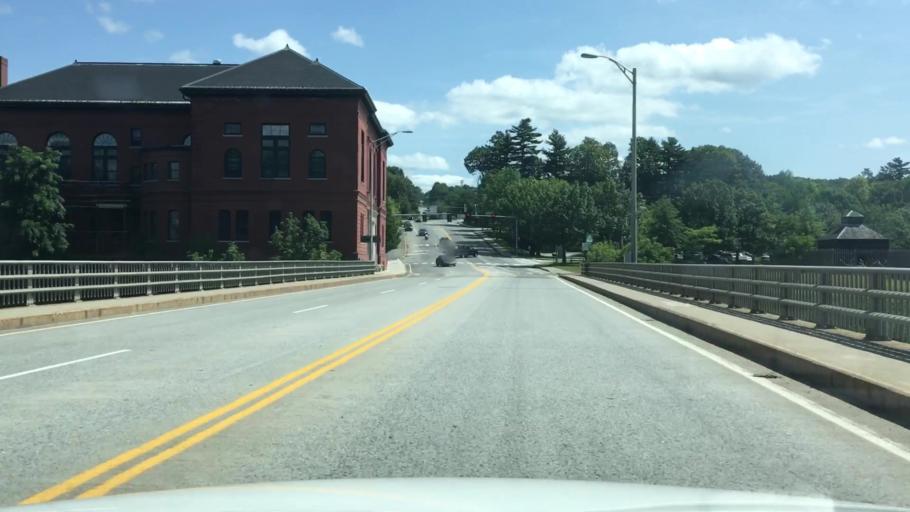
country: US
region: Maine
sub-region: Kennebec County
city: Augusta
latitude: 44.3167
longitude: -69.7722
